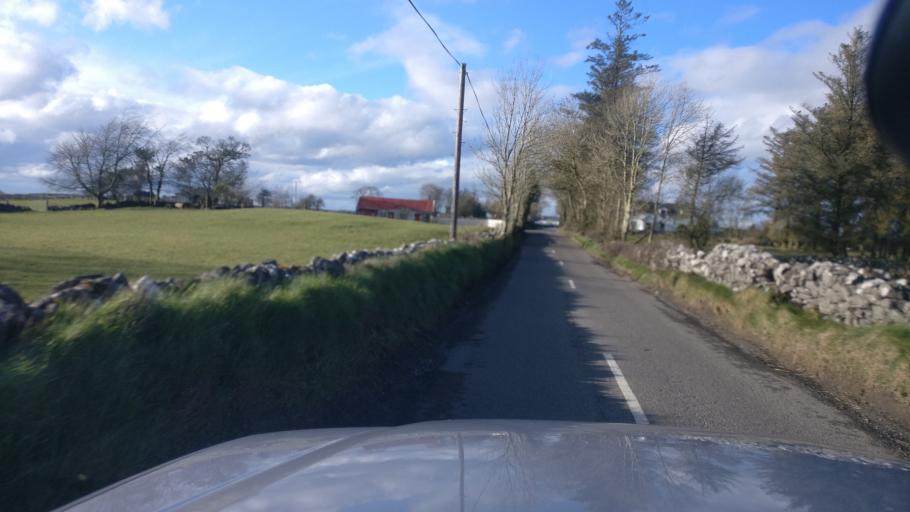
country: IE
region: Connaught
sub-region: County Galway
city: Loughrea
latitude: 53.1998
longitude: -8.4000
